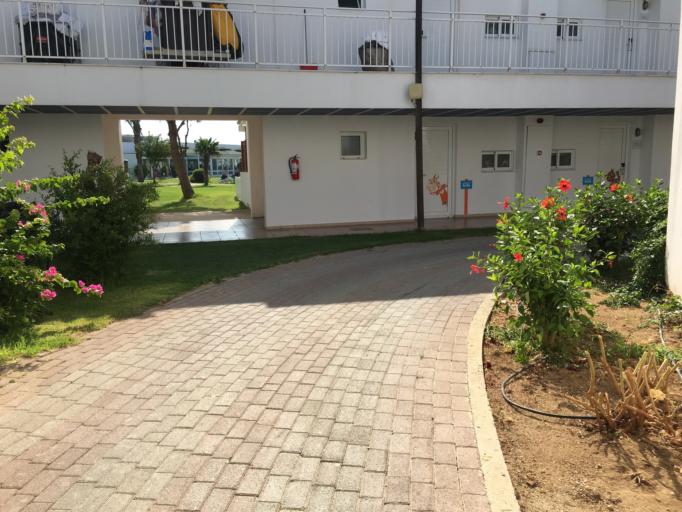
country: GR
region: South Aegean
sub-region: Nomos Dodekanisou
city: Rodos
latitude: 36.4059
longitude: 28.2261
